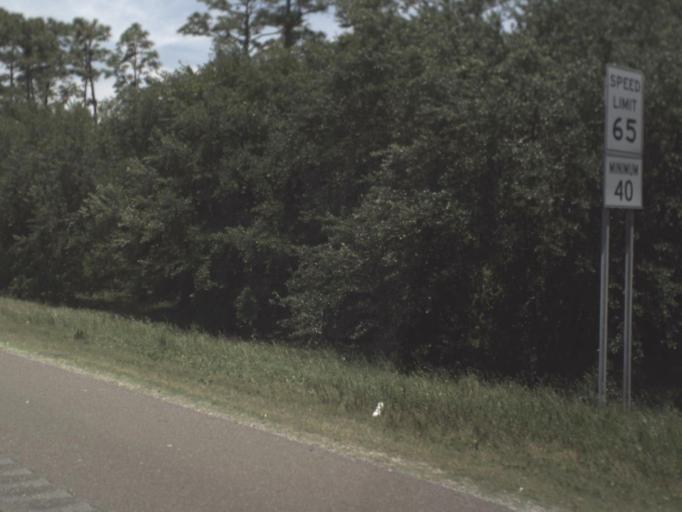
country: US
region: Florida
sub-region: Duval County
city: Jacksonville
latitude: 30.4235
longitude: -81.5691
